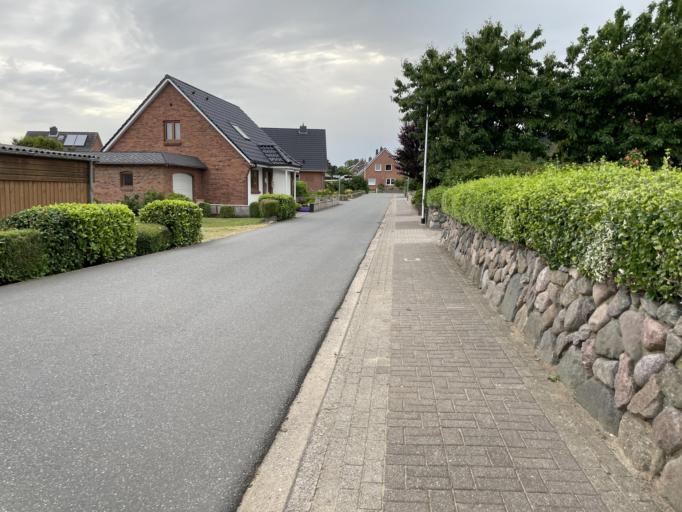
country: DE
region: Schleswig-Holstein
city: Mildstedt
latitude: 54.4621
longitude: 9.0930
